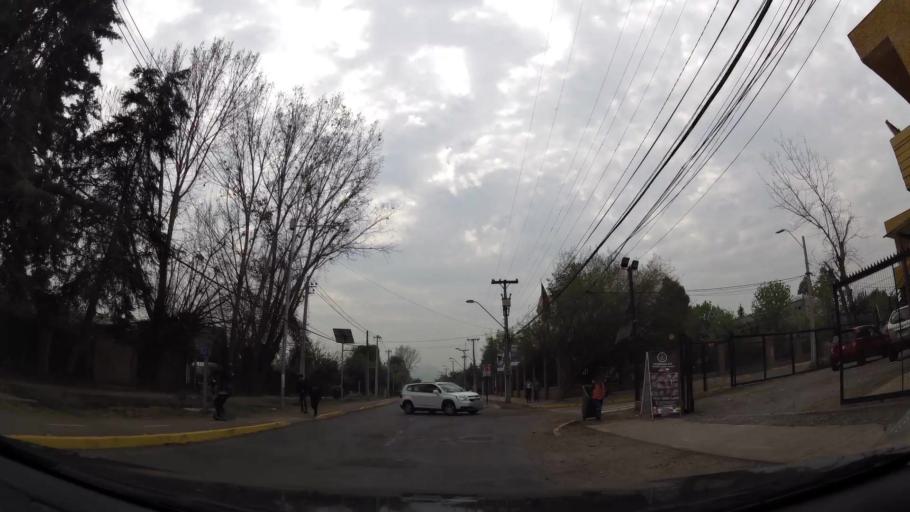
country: CL
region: Santiago Metropolitan
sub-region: Provincia de Chacabuco
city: Chicureo Abajo
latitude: -33.2010
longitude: -70.6790
